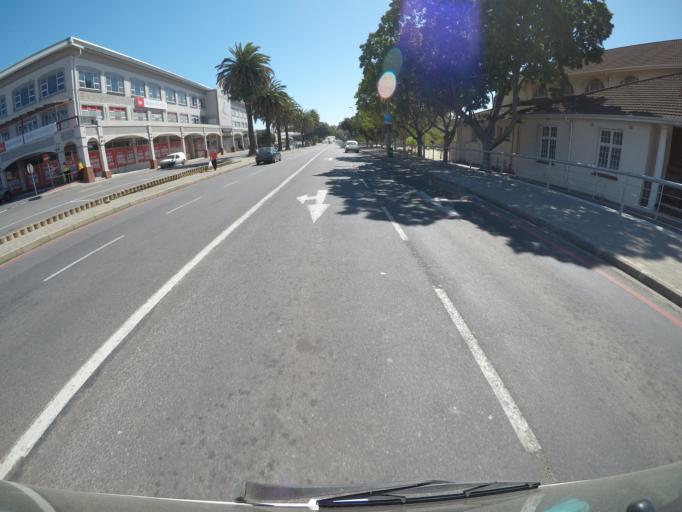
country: ZA
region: Western Cape
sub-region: City of Cape Town
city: Kraaifontein
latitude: -33.8336
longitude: 18.6482
